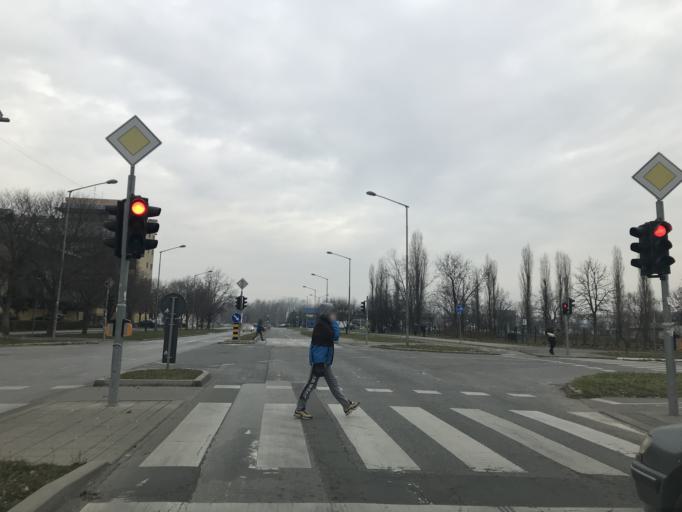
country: RS
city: Veternik
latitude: 45.2537
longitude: 19.7955
